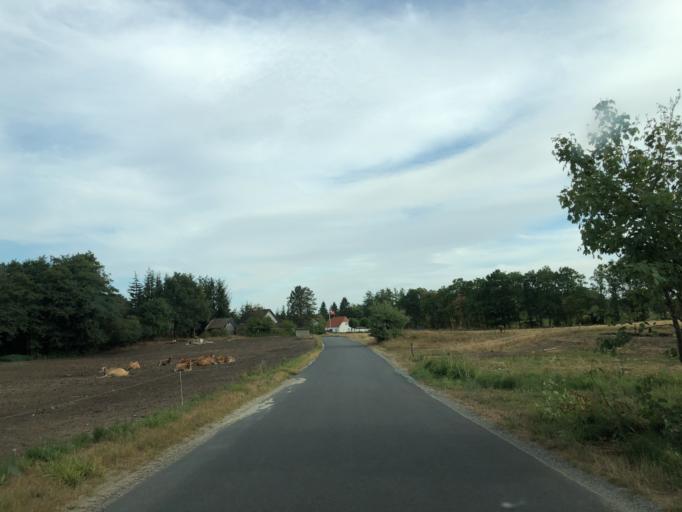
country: DK
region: South Denmark
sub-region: Vejle Kommune
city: Egtved
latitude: 55.6596
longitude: 9.2584
